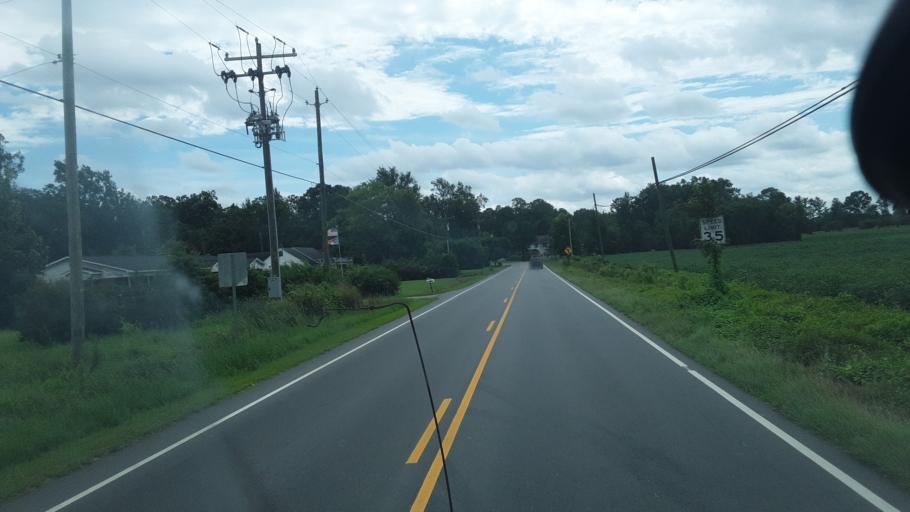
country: US
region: North Carolina
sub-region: Robeson County
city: Rowland
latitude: 34.5432
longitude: -79.3026
